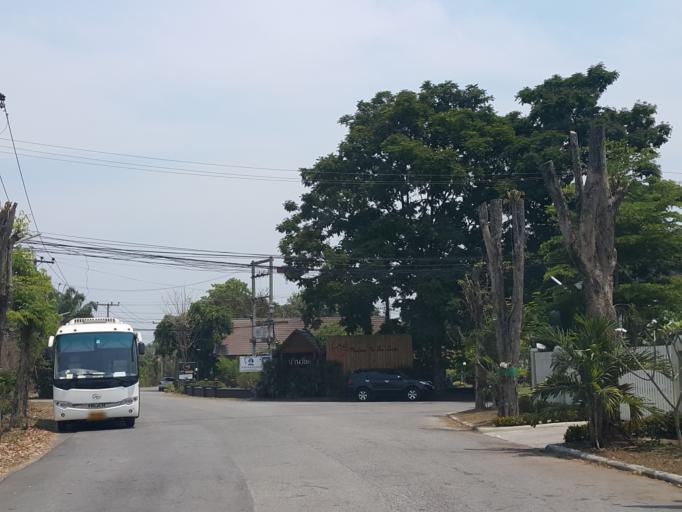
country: TH
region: Chiang Mai
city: Chiang Mai
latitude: 18.7333
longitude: 98.9735
